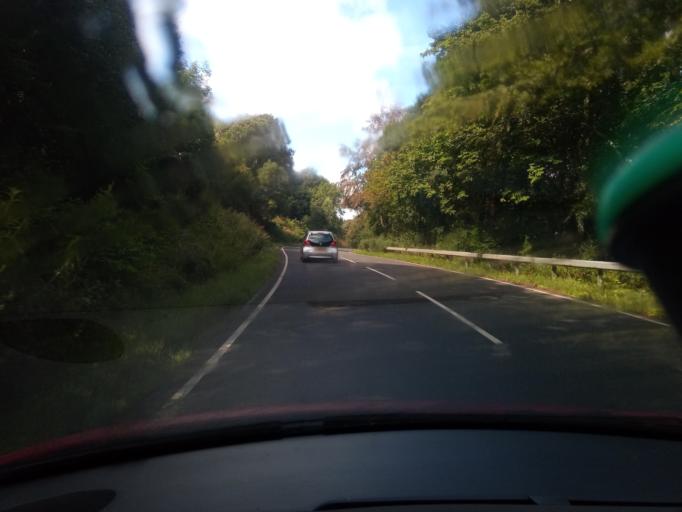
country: GB
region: Scotland
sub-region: The Scottish Borders
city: Jedburgh
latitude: 55.5713
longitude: -2.5375
